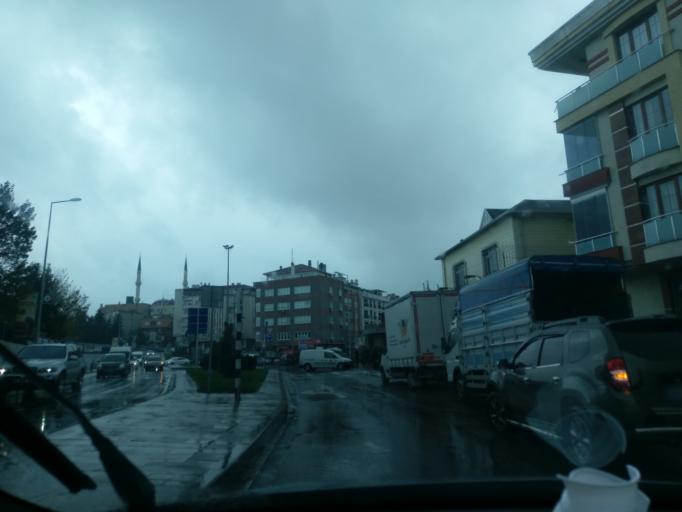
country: TR
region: Istanbul
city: Sisli
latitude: 41.0905
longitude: 28.9680
